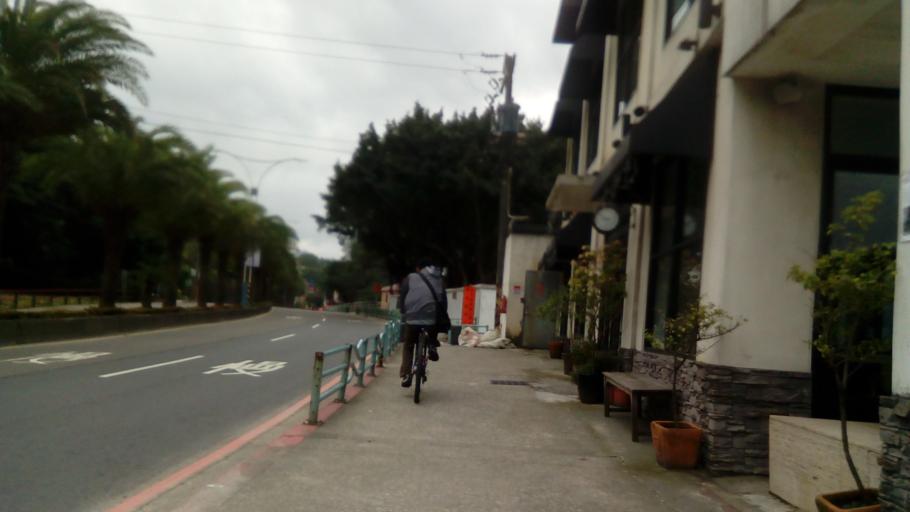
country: TW
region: Taipei
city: Taipei
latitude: 25.1751
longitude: 121.4312
